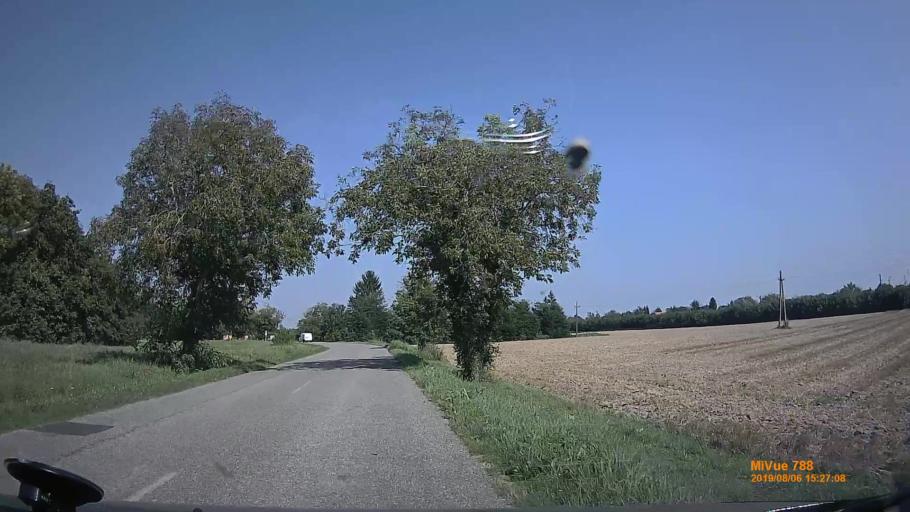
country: HR
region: Koprivnicko-Krizevacka
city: Drnje
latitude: 46.2514
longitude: 16.9660
